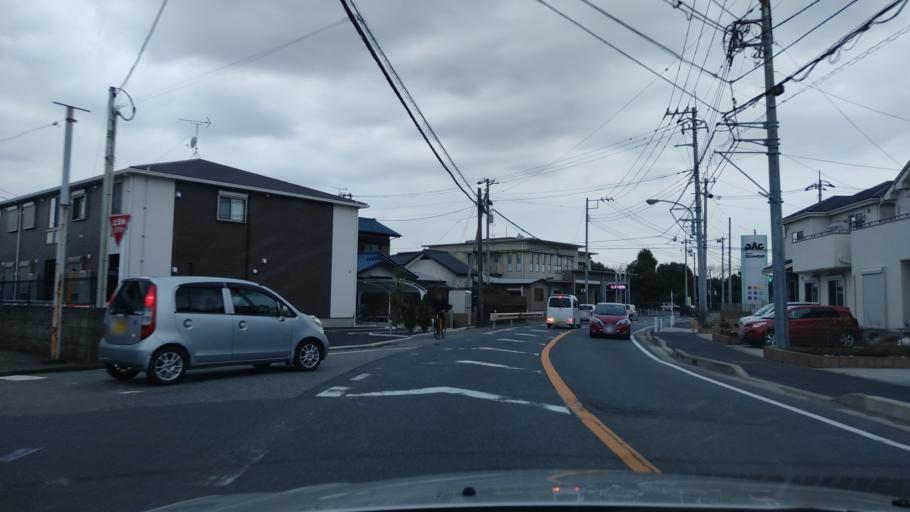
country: JP
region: Ibaraki
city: Moriya
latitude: 35.9135
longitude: 139.9475
